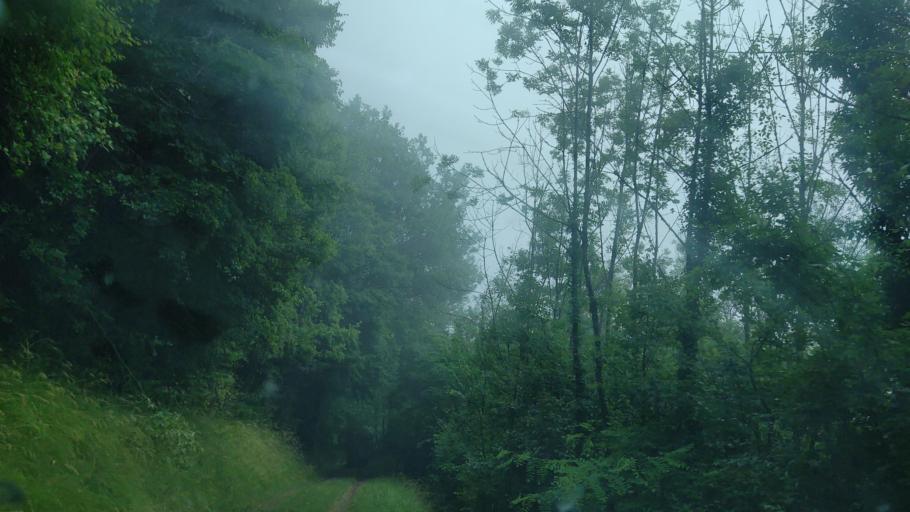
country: FR
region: Rhone-Alpes
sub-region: Departement de la Savoie
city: Coise-Saint-Jean-Pied-Gauthier
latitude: 45.4985
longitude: 6.1417
